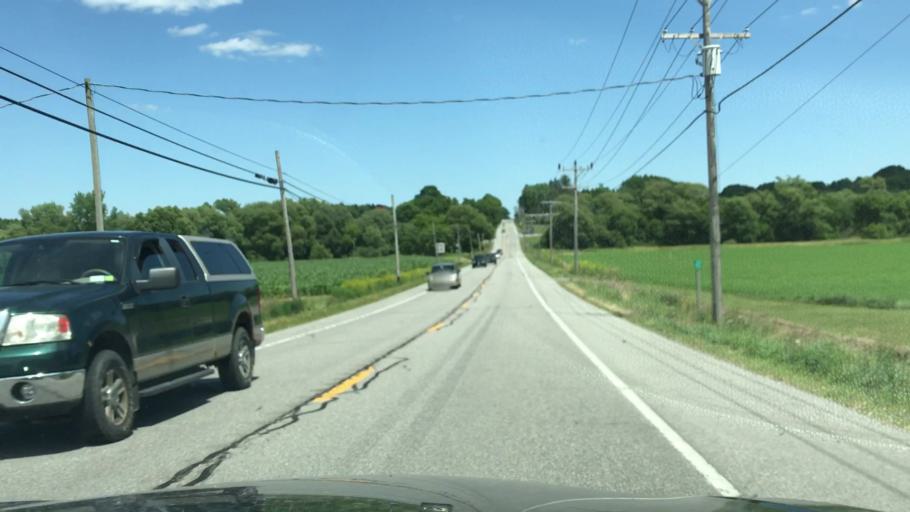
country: US
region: New York
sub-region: Wyoming County
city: Perry
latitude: 42.7460
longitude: -78.0388
